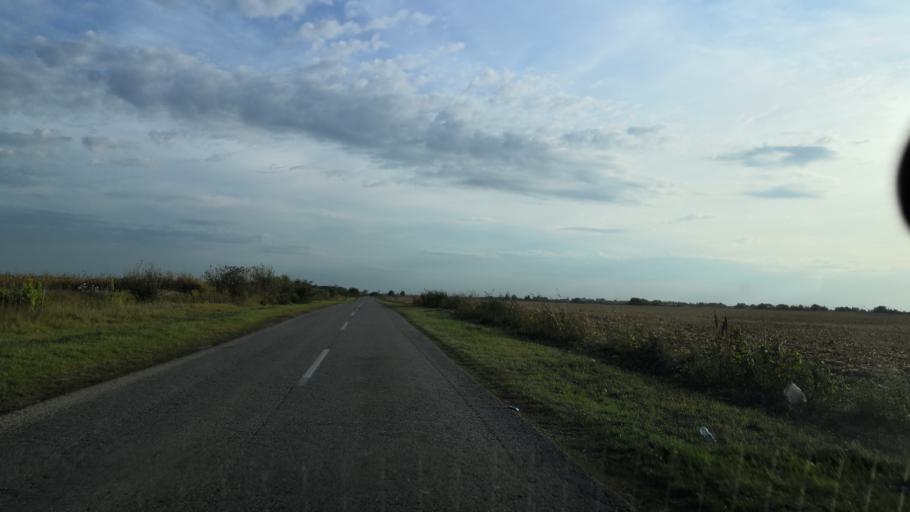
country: RS
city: Novi Karlovci
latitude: 45.0410
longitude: 20.1747
